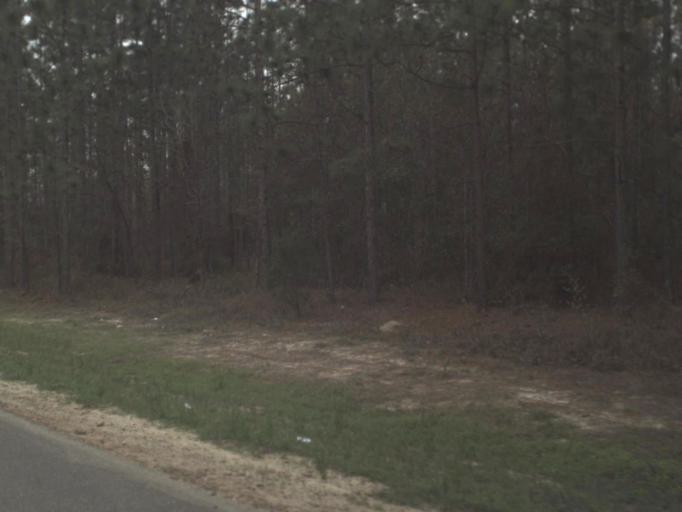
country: US
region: Florida
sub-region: Gadsden County
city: Gretna
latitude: 30.4895
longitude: -84.7213
